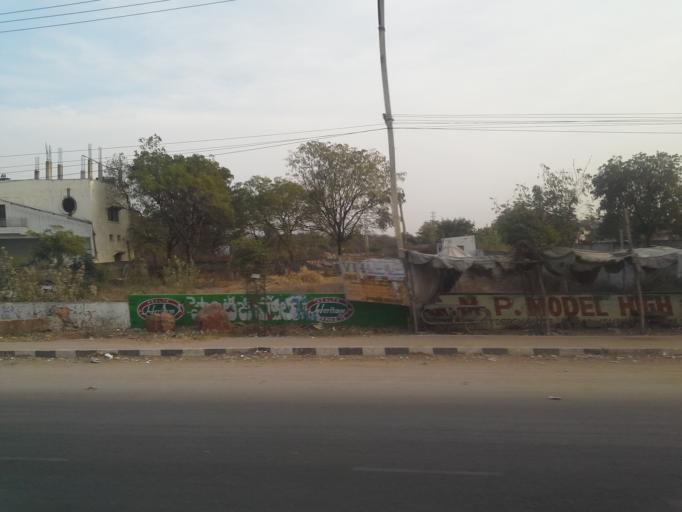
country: IN
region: Telangana
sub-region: Hyderabad
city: Hyderabad
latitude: 17.3590
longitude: 78.3871
